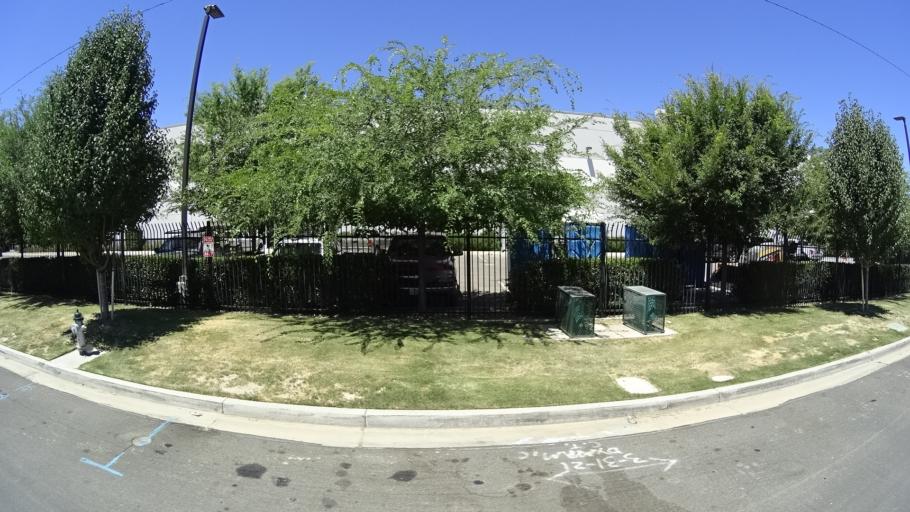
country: US
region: California
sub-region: Fresno County
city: Easton
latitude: 36.6877
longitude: -119.7681
